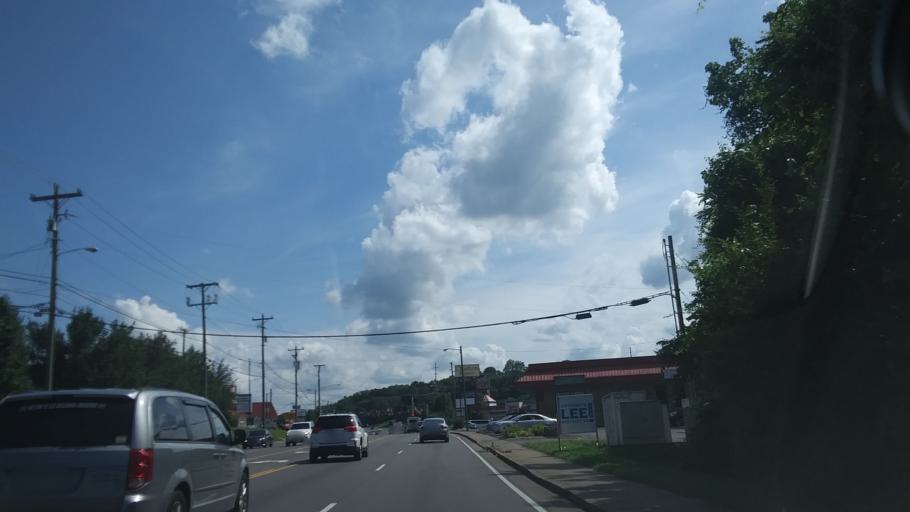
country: US
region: Tennessee
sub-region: Rutherford County
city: La Vergne
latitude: 36.0744
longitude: -86.6353
